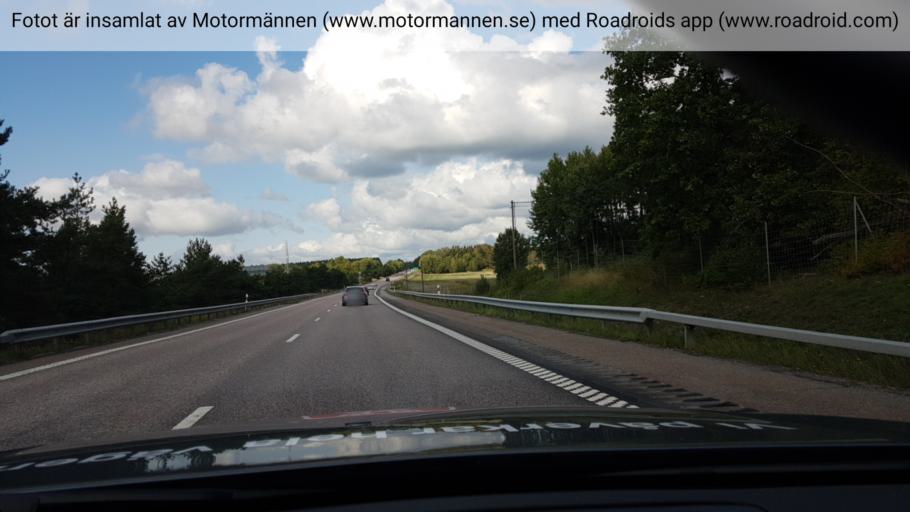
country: SE
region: Stockholm
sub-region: Sigtuna Kommun
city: Marsta
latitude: 59.6412
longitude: 17.8942
